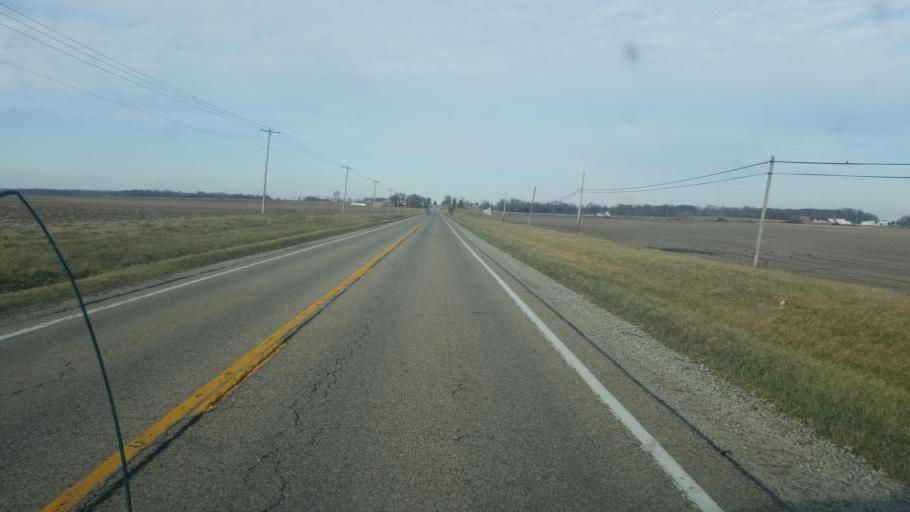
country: US
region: Illinois
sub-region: Lawrence County
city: Bridgeport
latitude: 38.5995
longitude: -87.6943
